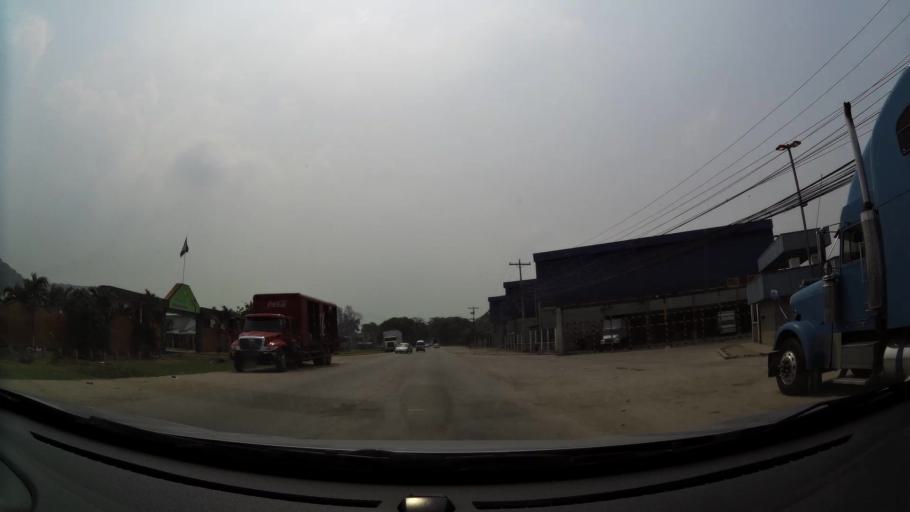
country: HN
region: Cortes
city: Chotepe
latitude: 15.4638
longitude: -87.9693
